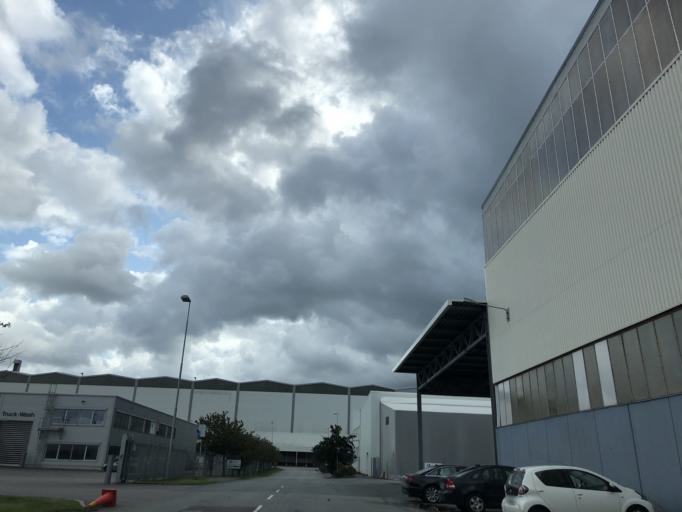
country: SE
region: Vaestra Goetaland
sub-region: Goteborg
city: Torslanda
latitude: 57.6996
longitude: 11.8210
